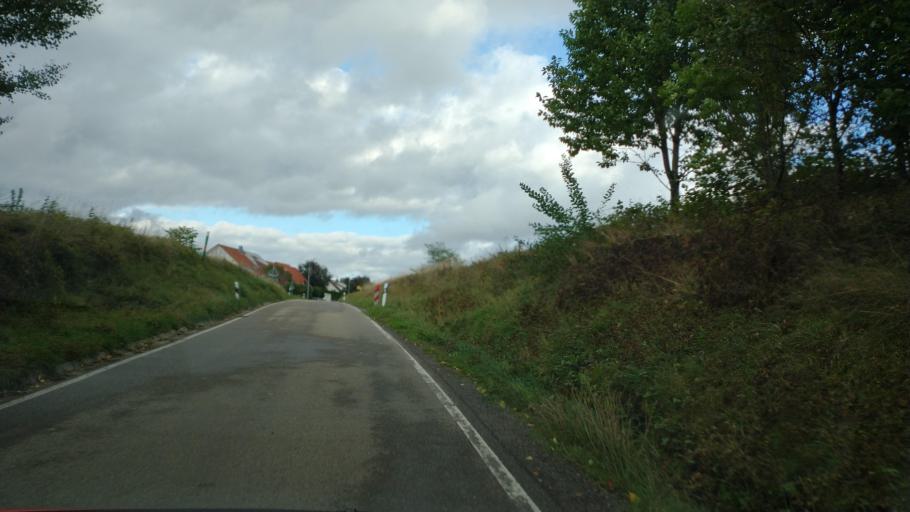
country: DE
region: Baden-Wuerttemberg
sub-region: Regierungsbezirk Stuttgart
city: Alfdorf
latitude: 48.8436
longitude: 9.7047
